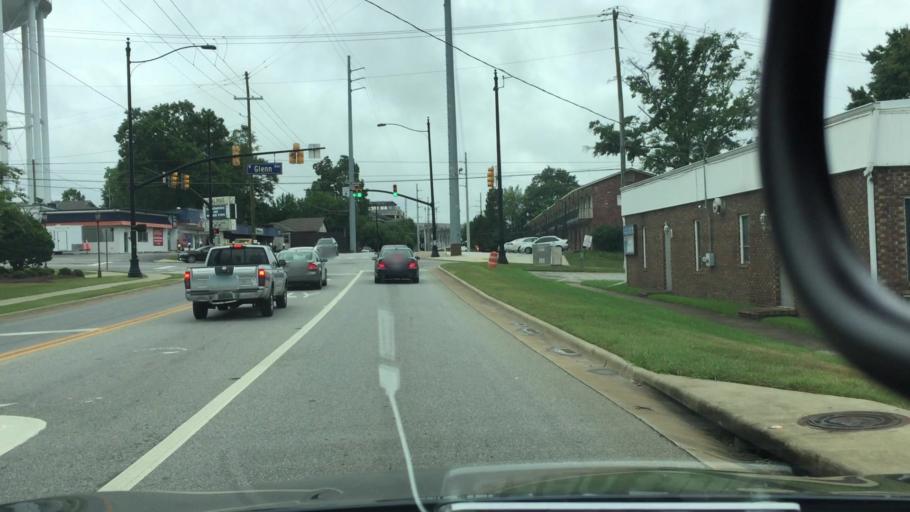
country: US
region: Alabama
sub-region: Lee County
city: Auburn
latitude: 32.6096
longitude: -85.4904
